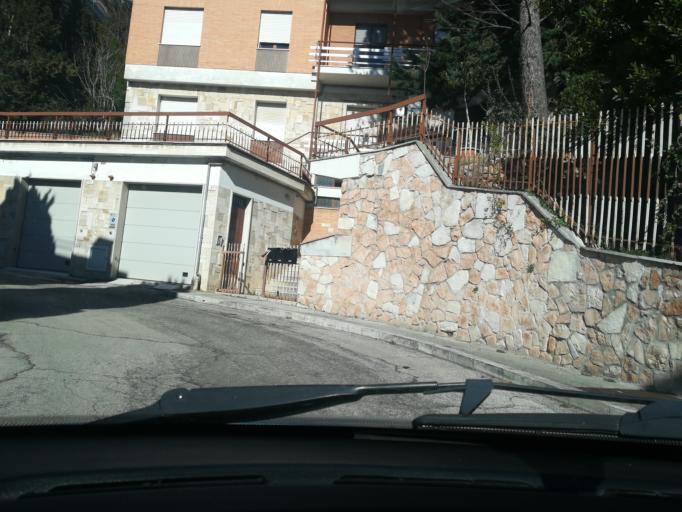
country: IT
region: The Marches
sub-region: Provincia di Macerata
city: Macerata
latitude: 43.2914
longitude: 13.4613
